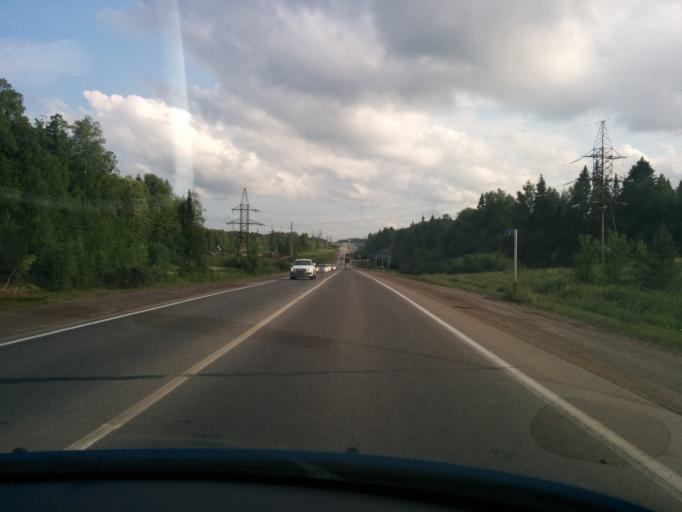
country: RU
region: Perm
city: Novyye Lyady
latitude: 58.0602
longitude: 56.4271
